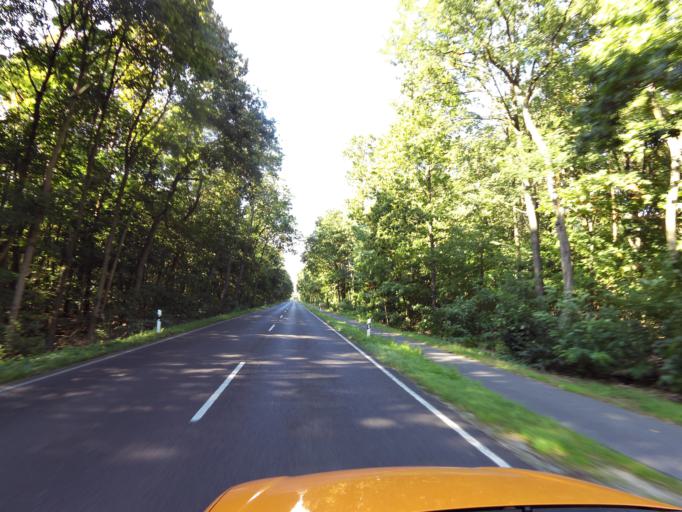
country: DE
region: Berlin
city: Wannsee
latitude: 52.3777
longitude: 13.1568
